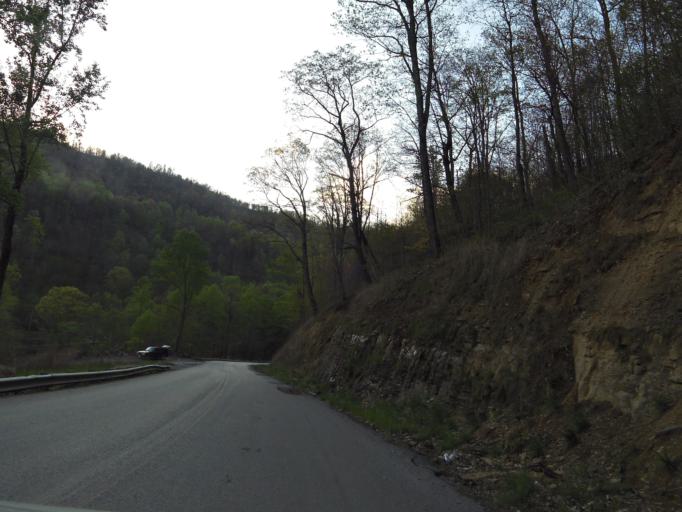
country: US
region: Kentucky
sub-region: Bell County
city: Middlesboro
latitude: 36.6228
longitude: -83.8769
